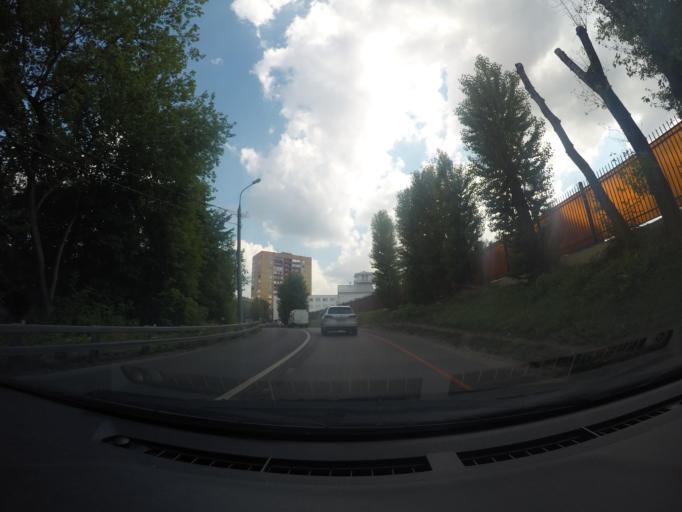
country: RU
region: Moscow
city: Sviblovo
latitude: 55.8396
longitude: 37.6299
